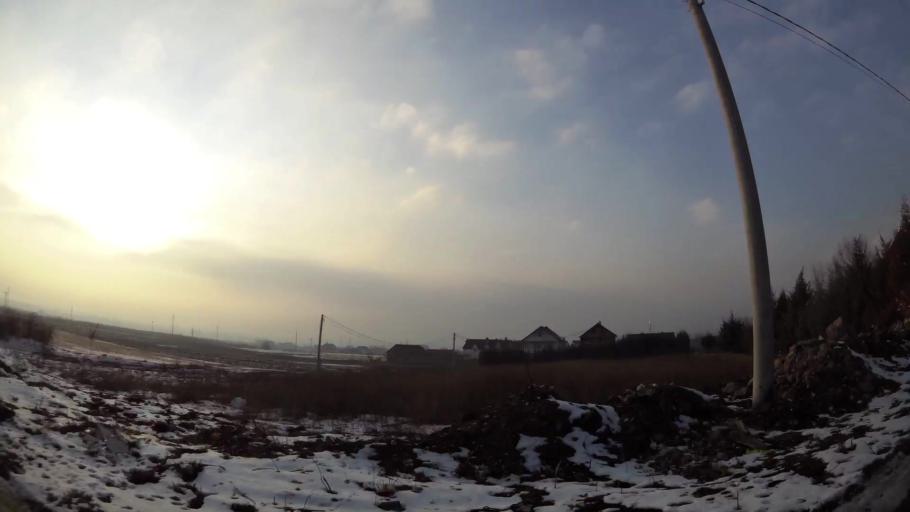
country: MK
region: Aracinovo
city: Arachinovo
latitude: 42.0192
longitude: 21.5677
